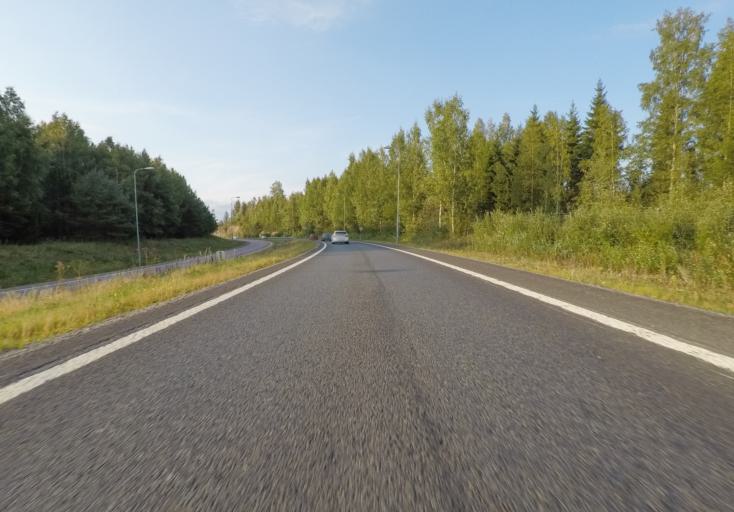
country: FI
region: Paijanne Tavastia
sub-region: Lahti
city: Heinola
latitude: 61.2882
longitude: 26.0770
